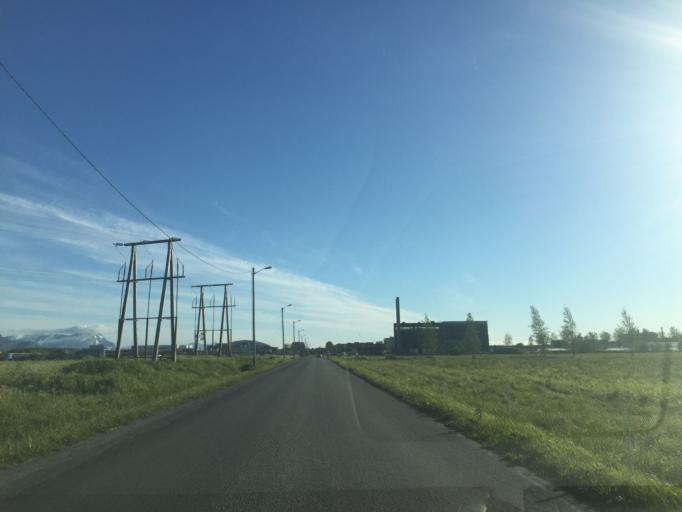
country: NO
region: Nordland
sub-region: Bodo
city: Bodo
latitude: 67.2835
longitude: 14.4339
